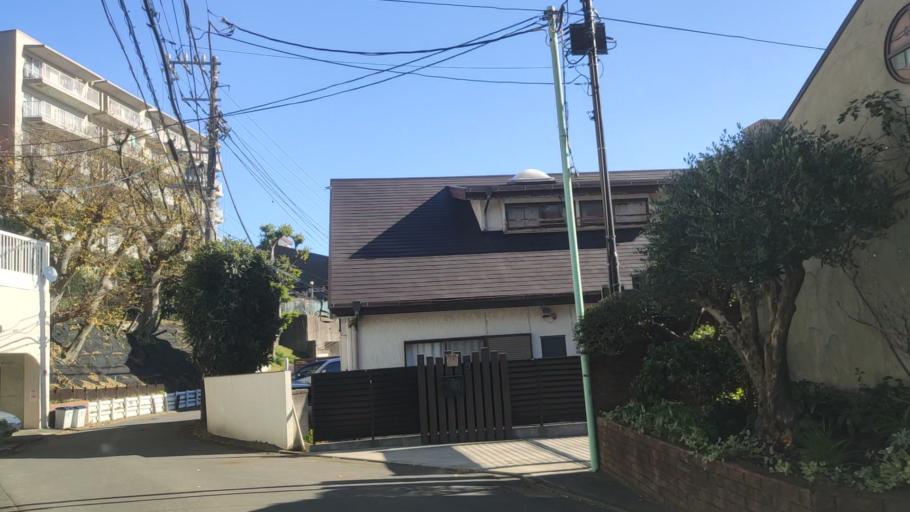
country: JP
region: Kanagawa
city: Yokohama
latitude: 35.4196
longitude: 139.6375
